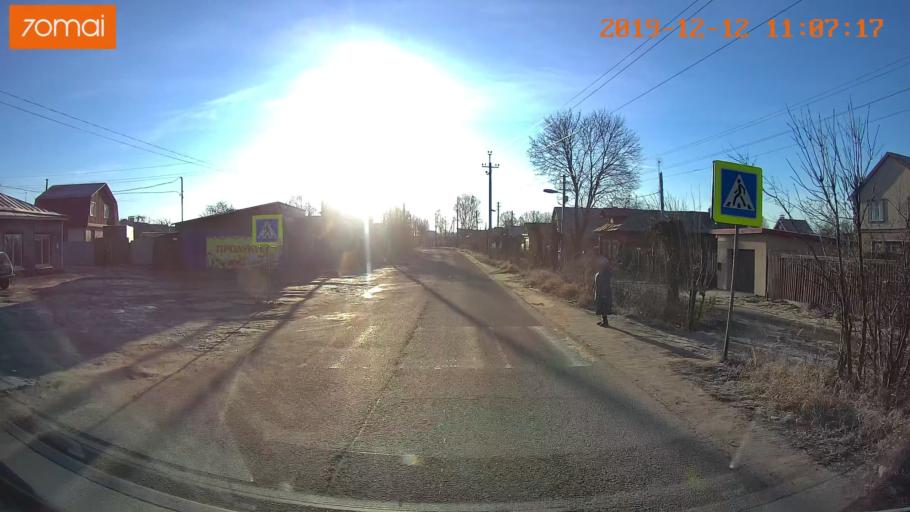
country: RU
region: Ivanovo
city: Kokhma
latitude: 56.9377
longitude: 41.0891
